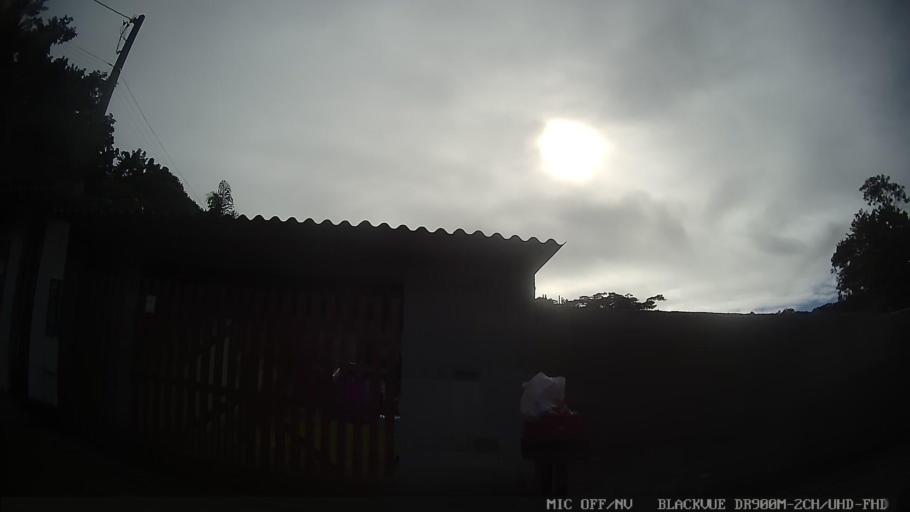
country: BR
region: Sao Paulo
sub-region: Peruibe
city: Peruibe
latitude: -24.2279
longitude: -46.9166
